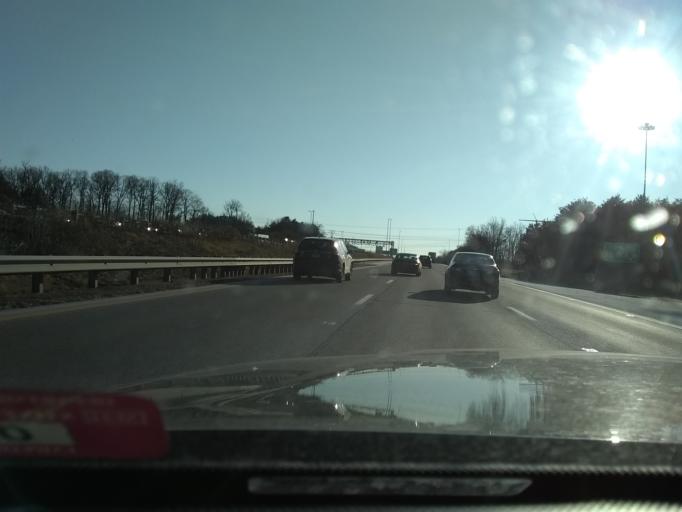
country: US
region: Virginia
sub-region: Prince William County
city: Potomac Mills
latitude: 38.6558
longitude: -77.2804
